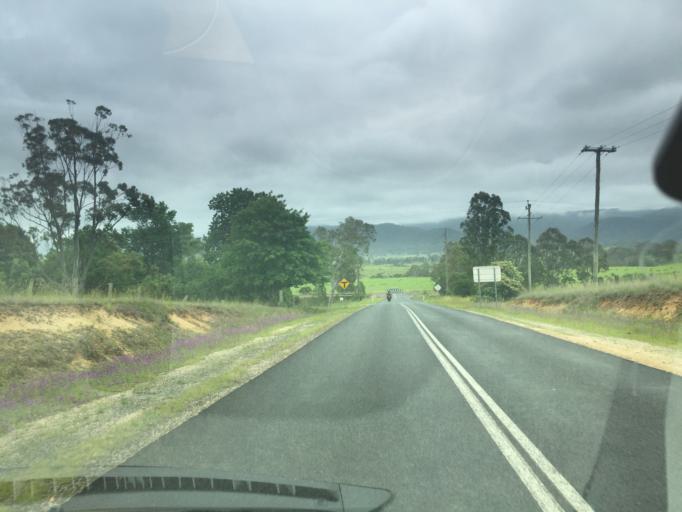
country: AU
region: New South Wales
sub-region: Bega Valley
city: Bega
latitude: -36.6460
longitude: 149.5856
